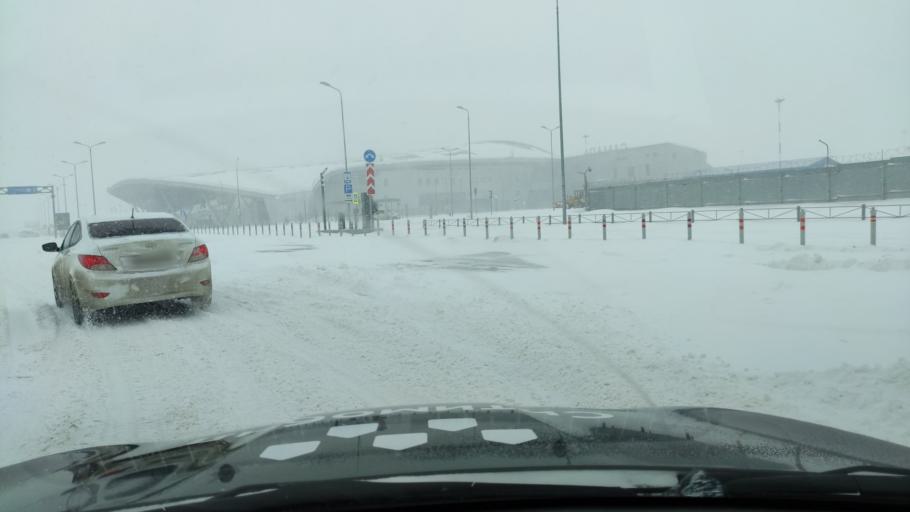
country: RU
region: Samara
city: Bereza
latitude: 53.5122
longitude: 50.1535
